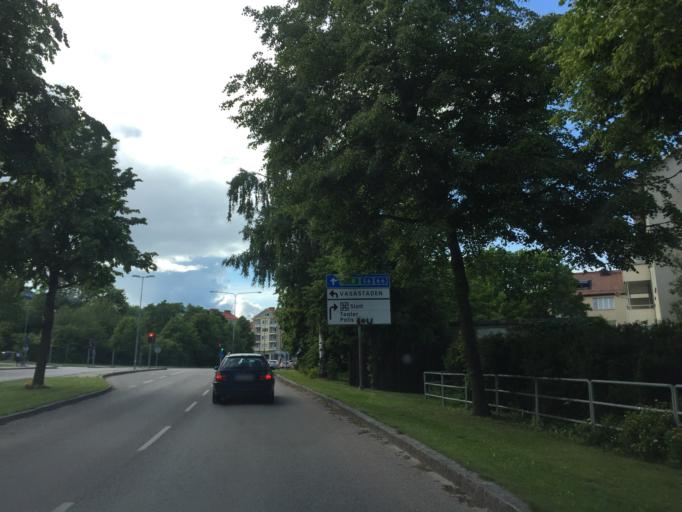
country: SE
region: Vaestmanland
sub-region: Vasteras
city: Vasteras
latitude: 59.6069
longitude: 16.5413
